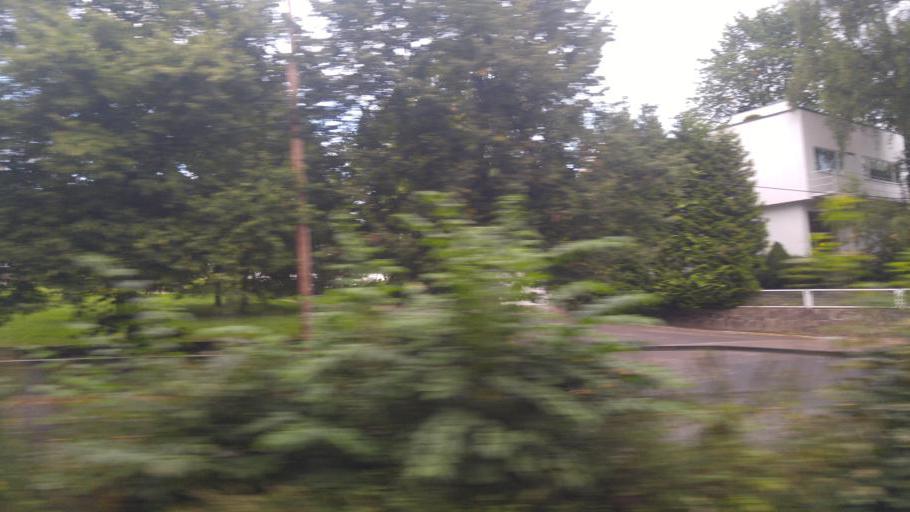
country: NO
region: Oslo
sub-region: Oslo
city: Sjolyststranda
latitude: 59.9365
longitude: 10.7074
